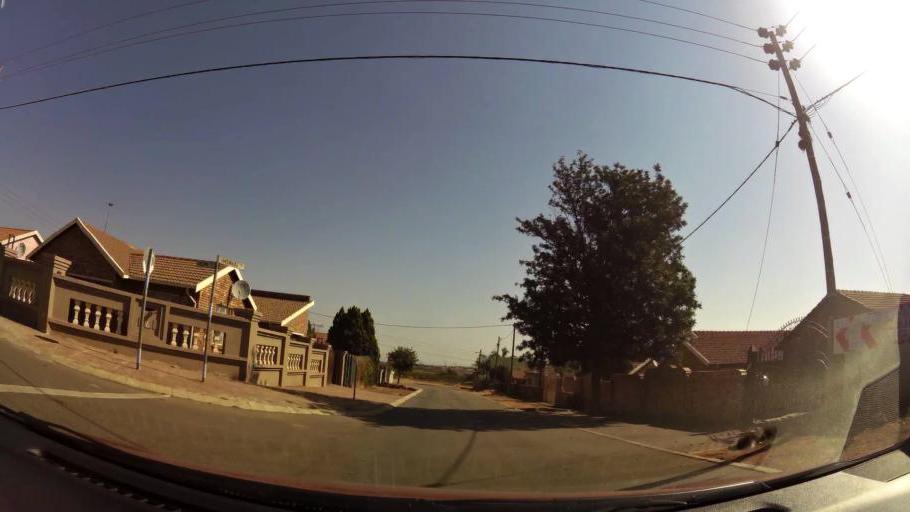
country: ZA
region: Gauteng
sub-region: City of Tshwane Metropolitan Municipality
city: Mabopane
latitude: -25.5520
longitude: 28.0786
